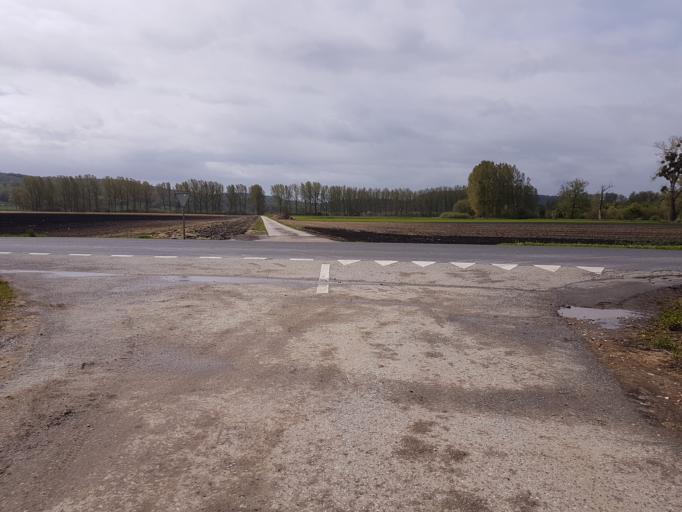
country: CH
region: Vaud
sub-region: Jura-Nord vaudois District
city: Bavois
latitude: 46.6886
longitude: 6.5537
